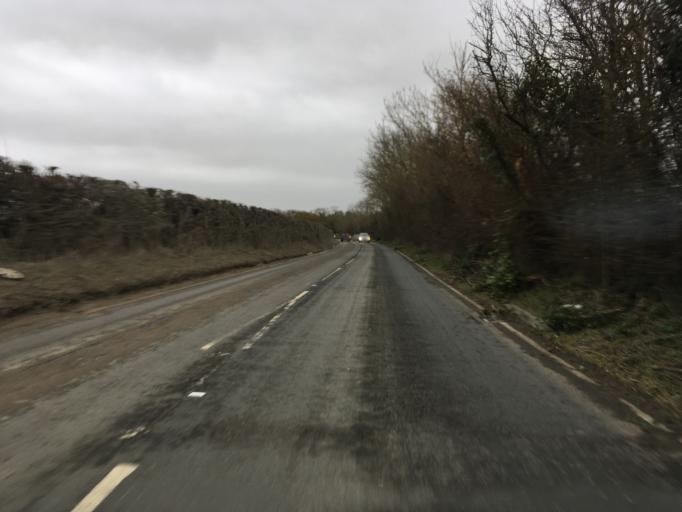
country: GB
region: England
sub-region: Oxfordshire
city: Wantage
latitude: 51.5960
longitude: -1.4635
